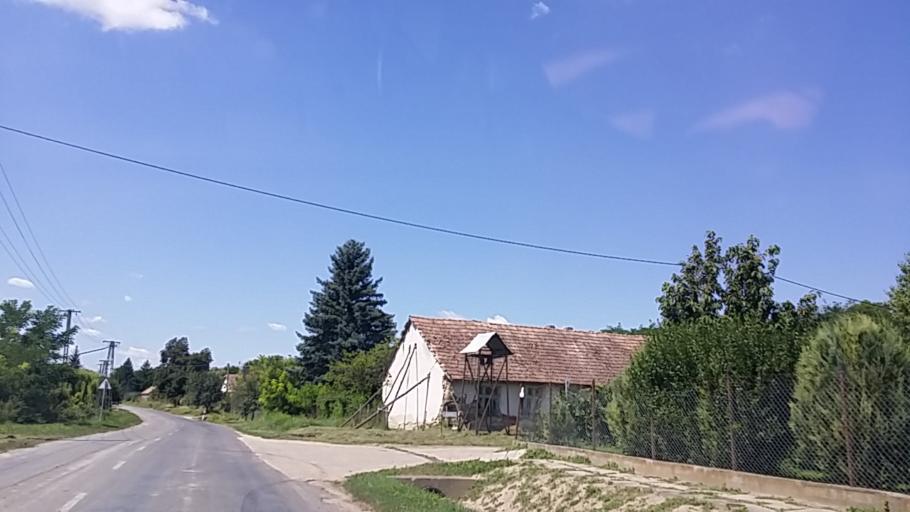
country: HU
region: Tolna
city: Ozora
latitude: 46.7490
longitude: 18.4629
